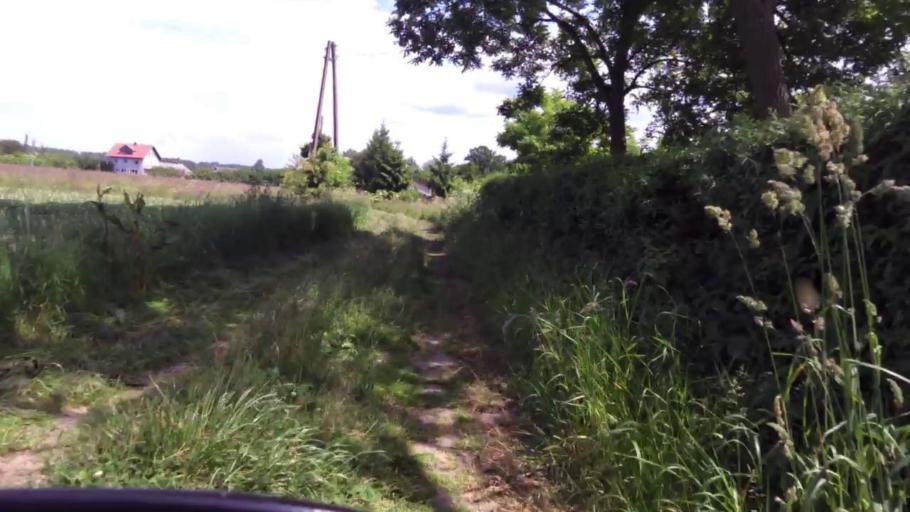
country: PL
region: West Pomeranian Voivodeship
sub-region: Powiat kamienski
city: Wolin
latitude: 53.8507
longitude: 14.5785
